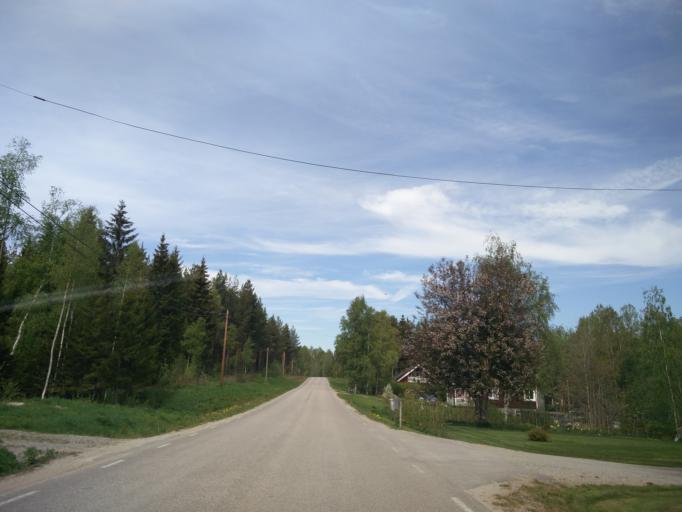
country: SE
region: Gaevleborg
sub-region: Hudiksvalls Kommun
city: Sorforsa
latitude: 61.6839
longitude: 16.9244
